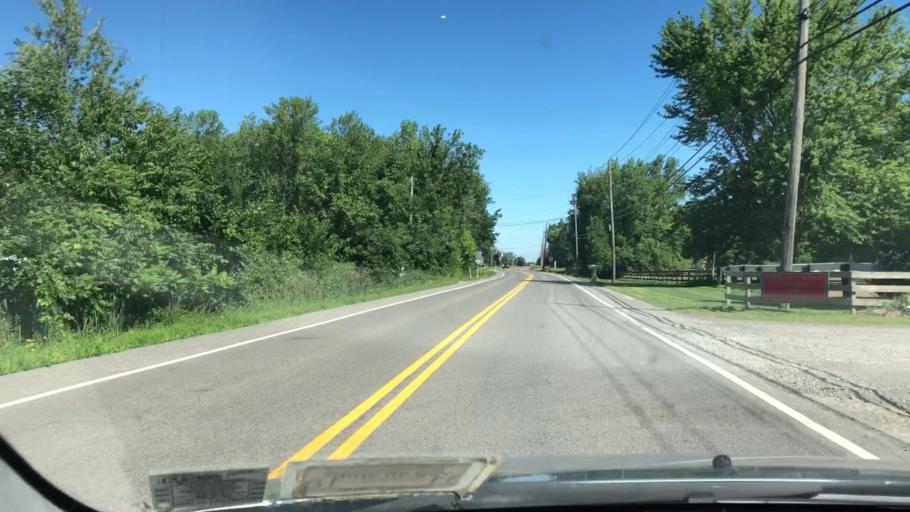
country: US
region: New York
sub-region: Monroe County
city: Webster
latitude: 43.1949
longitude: -77.4003
